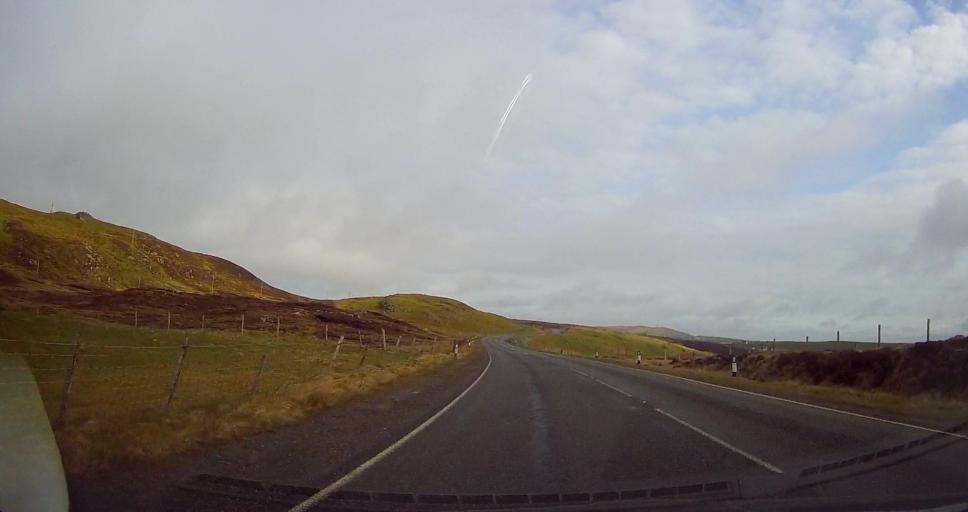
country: GB
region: Scotland
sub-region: Shetland Islands
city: Lerwick
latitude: 60.1064
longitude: -1.2193
